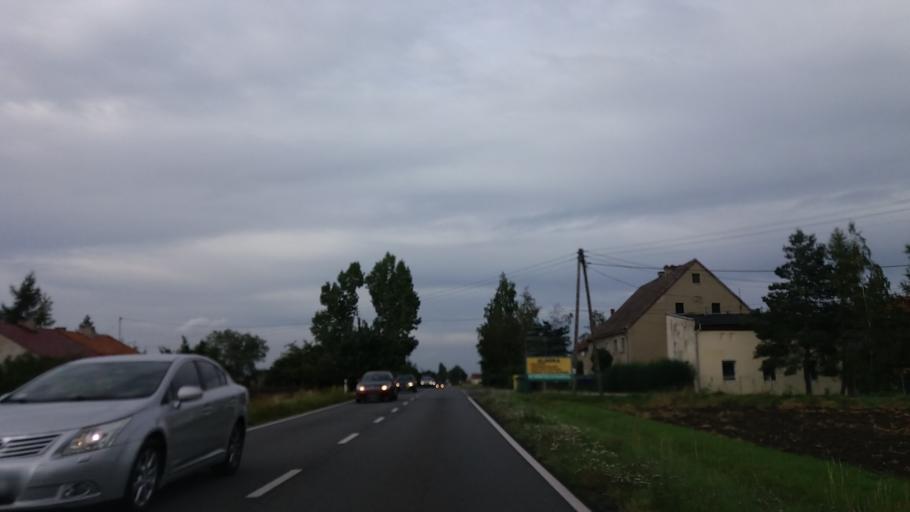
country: PL
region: Lower Silesian Voivodeship
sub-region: Powiat swidnicki
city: Stanowice
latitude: 50.9031
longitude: 16.3561
